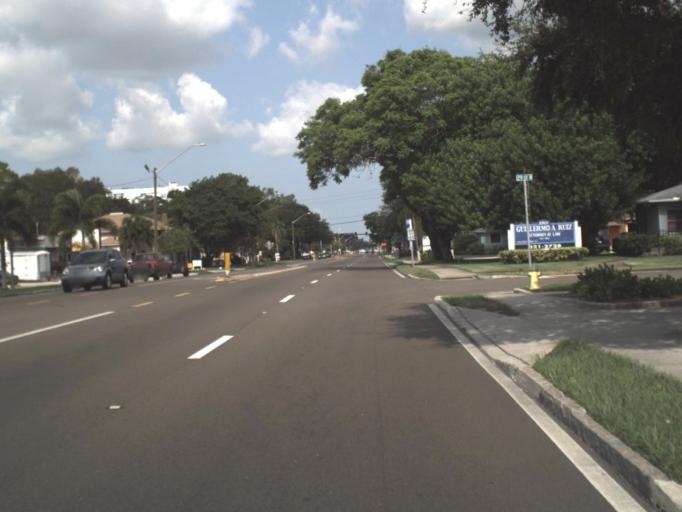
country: US
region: Florida
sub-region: Pinellas County
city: Saint Petersburg
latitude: 27.7774
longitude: -82.6723
